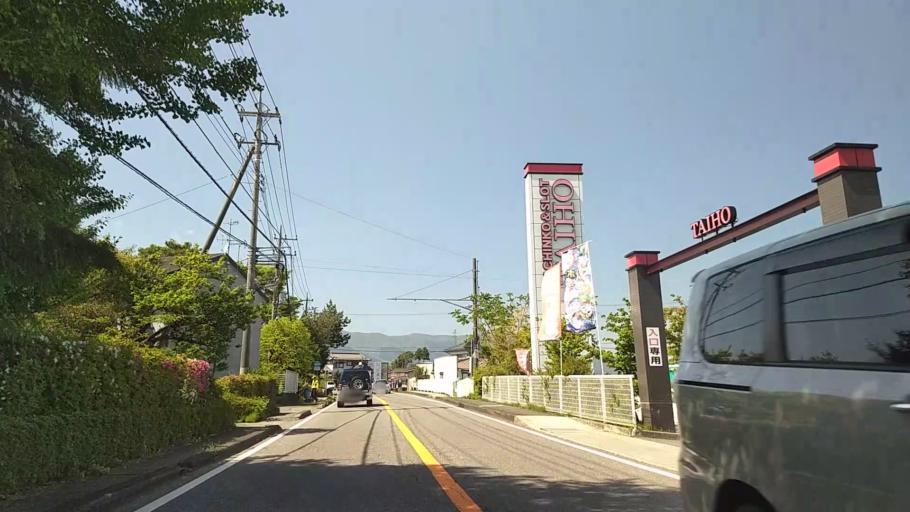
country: JP
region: Shizuoka
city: Gotemba
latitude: 35.3115
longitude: 138.9221
